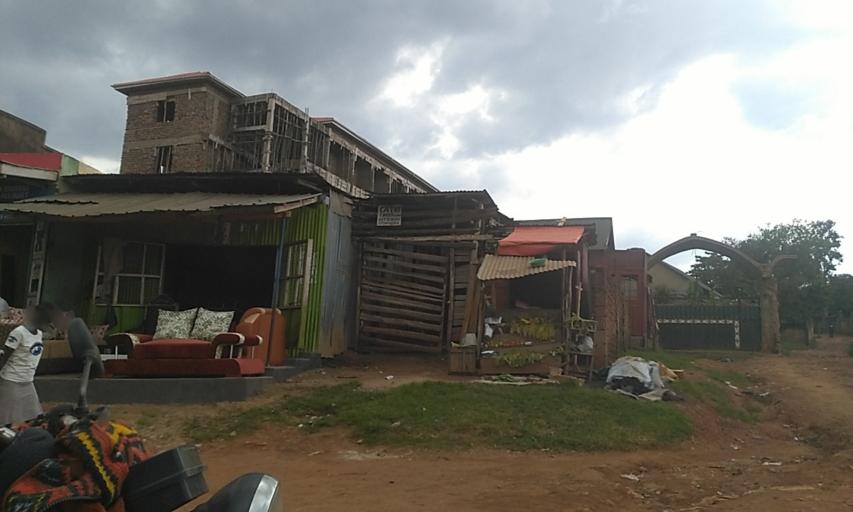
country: UG
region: Central Region
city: Kampala Central Division
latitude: 0.3226
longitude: 32.5038
